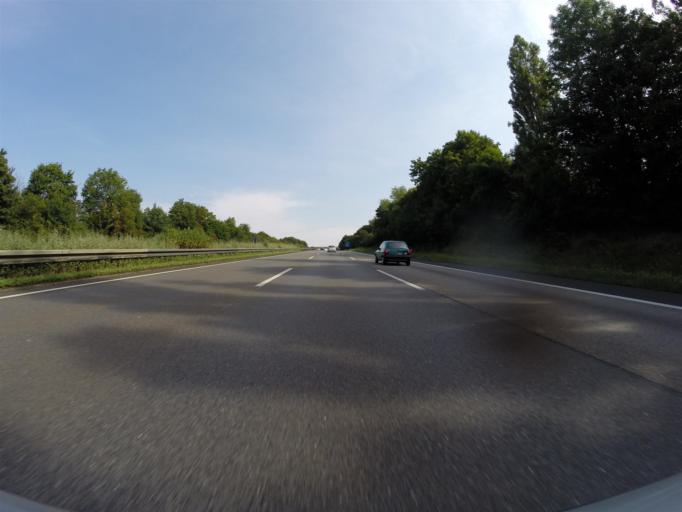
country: DE
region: Hesse
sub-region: Regierungsbezirk Kassel
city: Guxhagen
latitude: 51.2253
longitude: 9.4809
